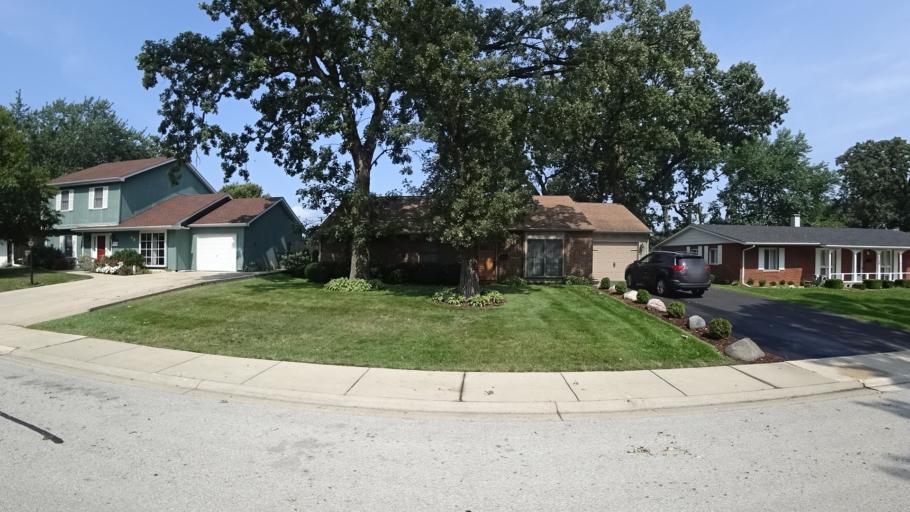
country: US
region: Illinois
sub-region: Cook County
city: Orland Park
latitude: 41.6196
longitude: -87.8681
